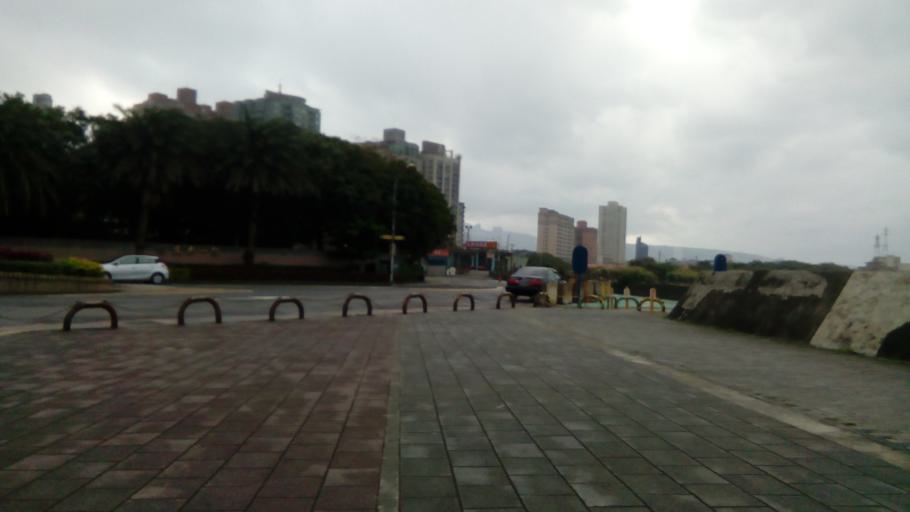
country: TW
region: Taipei
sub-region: Taipei
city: Banqiao
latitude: 25.1813
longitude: 121.4166
